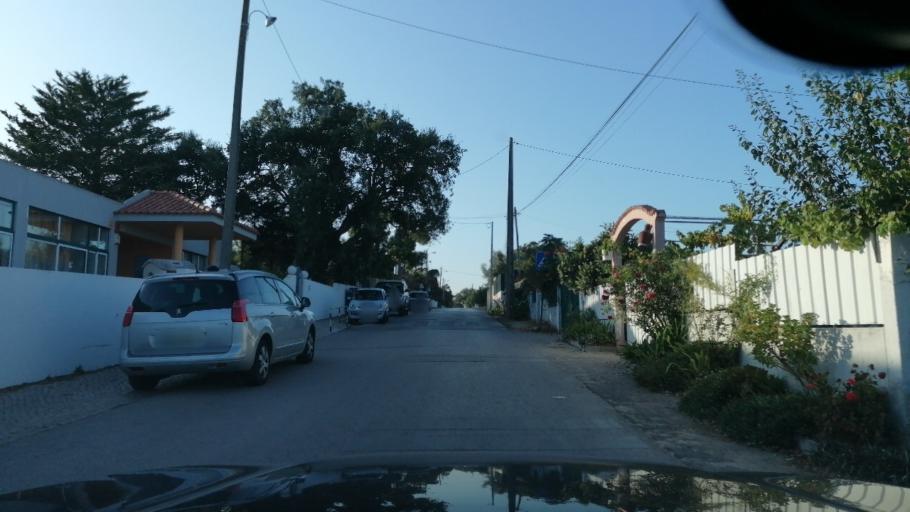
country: PT
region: Setubal
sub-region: Setubal
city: Setubal
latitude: 38.5443
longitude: -8.8394
